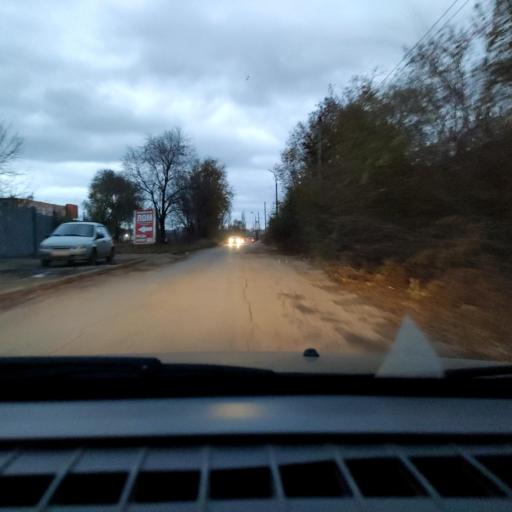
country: RU
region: Samara
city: Tol'yatti
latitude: 53.5616
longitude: 49.3127
